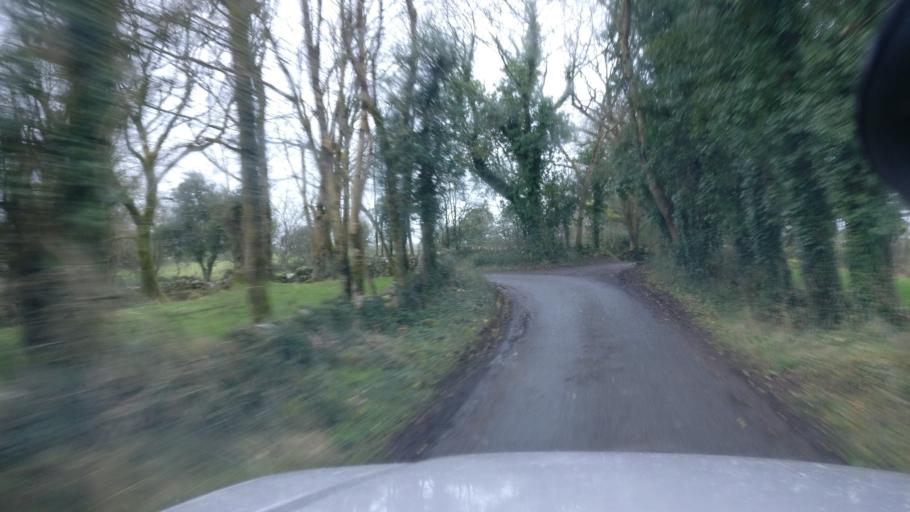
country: IE
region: Connaught
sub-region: County Galway
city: Loughrea
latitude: 53.2249
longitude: -8.5953
